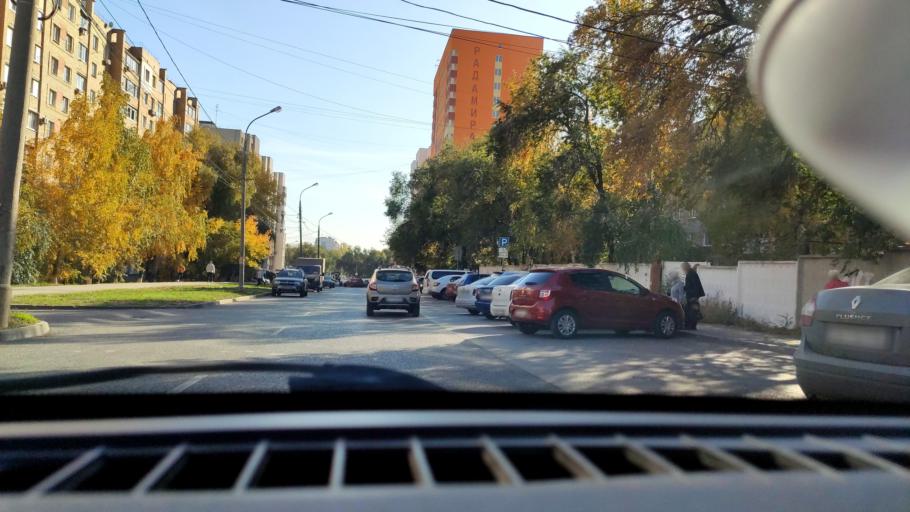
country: RU
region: Samara
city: Samara
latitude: 53.2093
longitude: 50.2207
